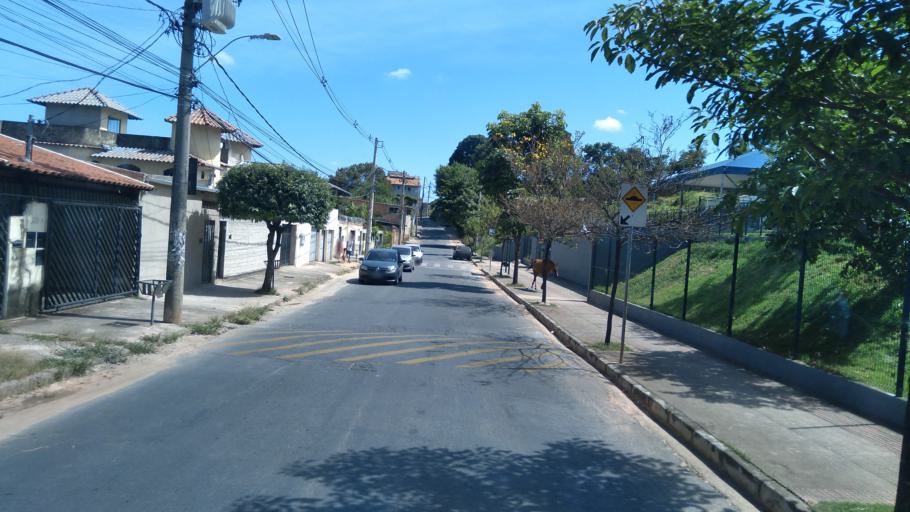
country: BR
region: Minas Gerais
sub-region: Belo Horizonte
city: Belo Horizonte
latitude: -19.8467
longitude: -43.9007
